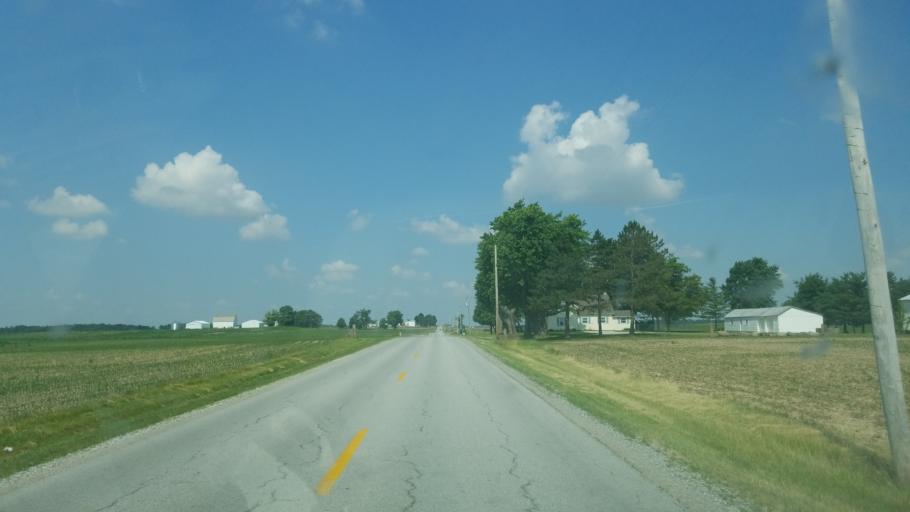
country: US
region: Ohio
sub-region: Auglaize County
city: Wapakoneta
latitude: 40.5707
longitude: -84.1113
